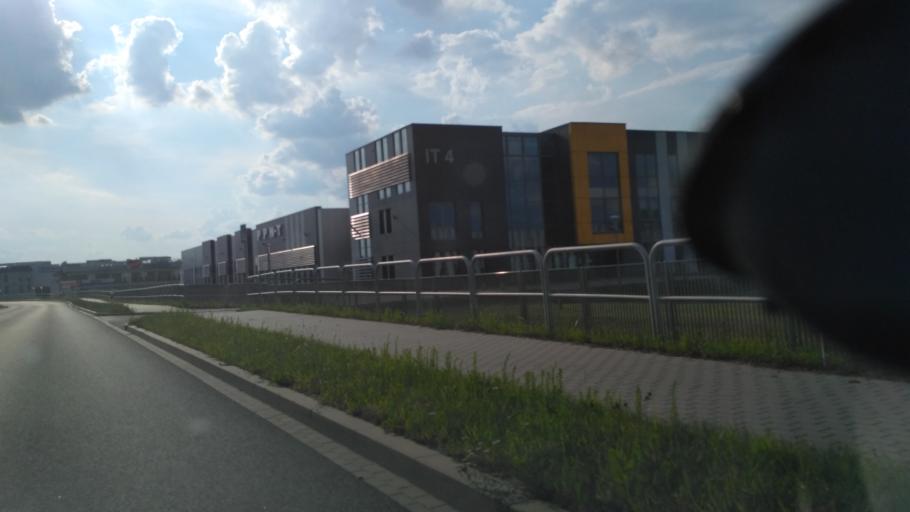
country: PL
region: Subcarpathian Voivodeship
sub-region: Powiat rzeszowski
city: Trzebownisko
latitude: 50.1160
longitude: 22.0144
